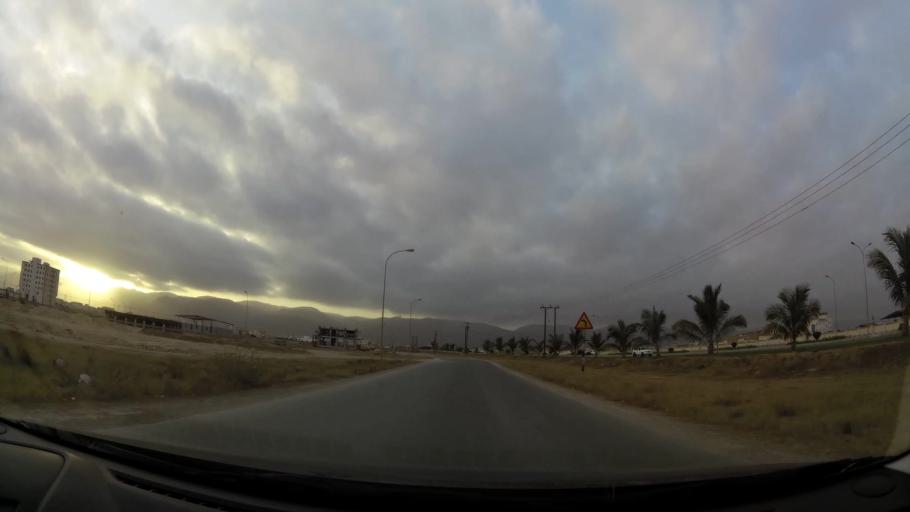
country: OM
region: Zufar
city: Salalah
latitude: 17.0283
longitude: 54.0307
